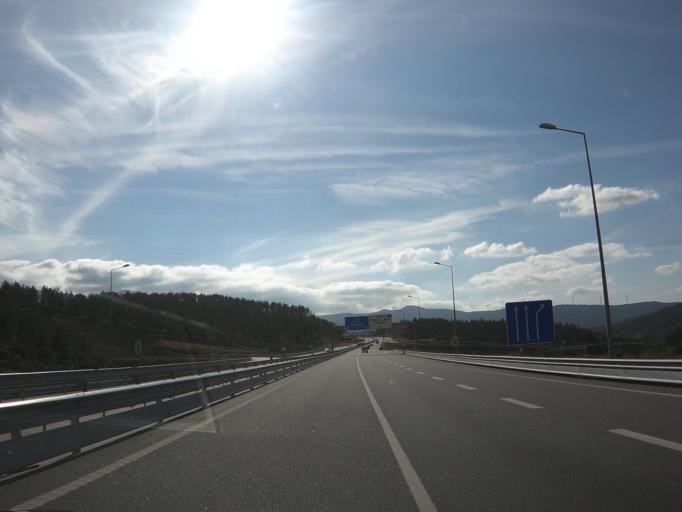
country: PT
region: Vila Real
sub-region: Santa Marta de Penaguiao
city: Santa Marta de Penaguiao
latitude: 41.2785
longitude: -7.8308
